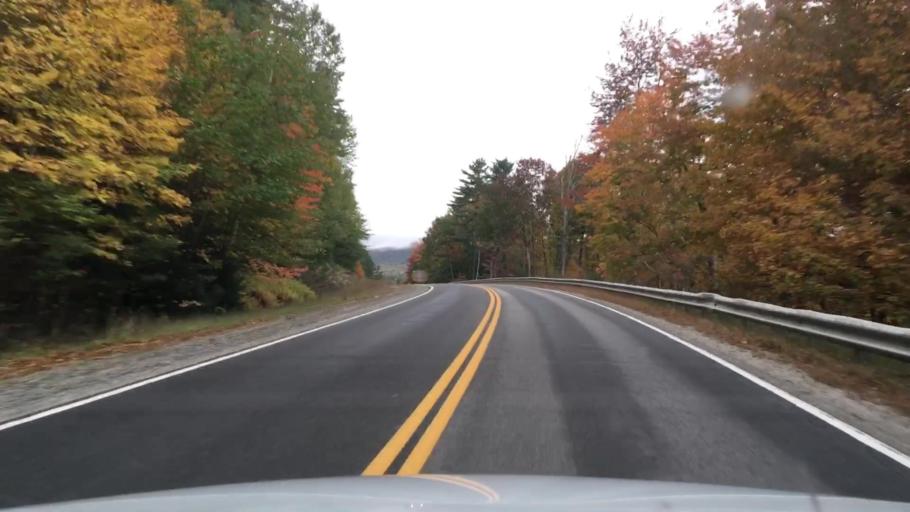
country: US
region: Maine
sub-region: Oxford County
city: Bethel
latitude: 44.4061
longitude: -70.7986
